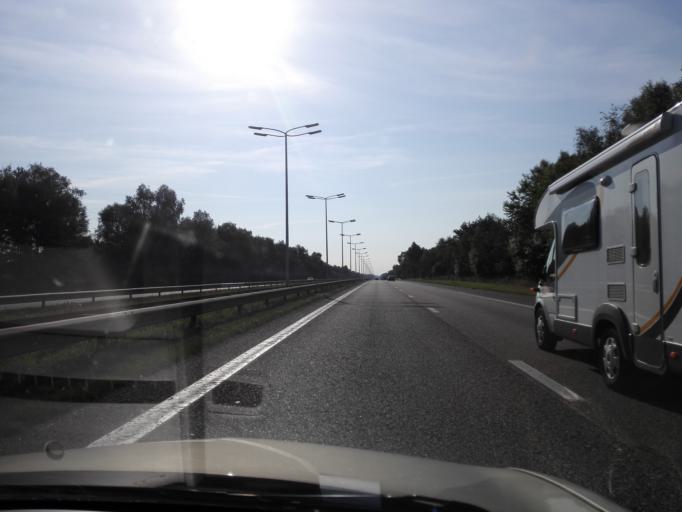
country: BE
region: Flanders
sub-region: Provincie Limburg
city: Houthalen
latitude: 51.0103
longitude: 5.4187
